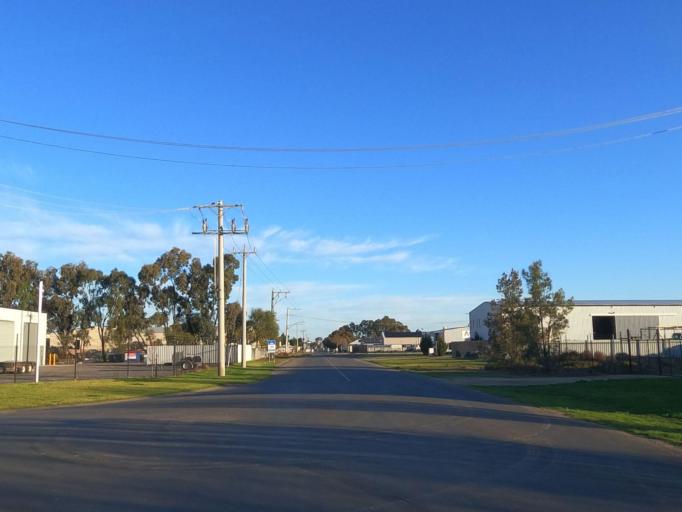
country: AU
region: Victoria
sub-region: Swan Hill
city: Swan Hill
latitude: -35.3270
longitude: 143.5351
